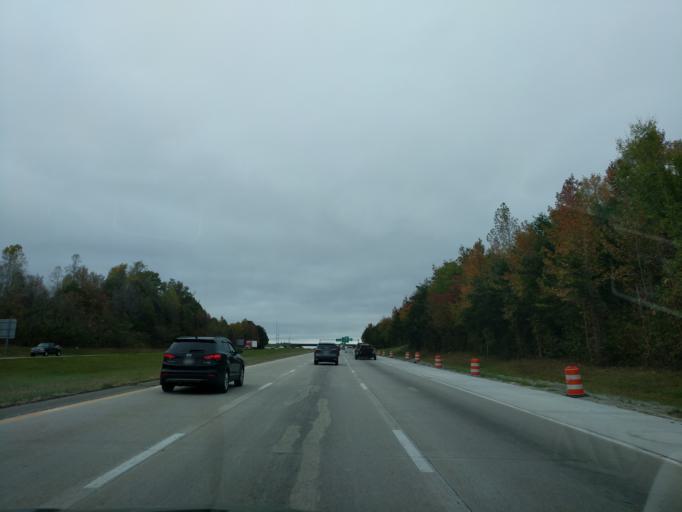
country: US
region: North Carolina
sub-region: Randolph County
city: Archdale
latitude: 35.9185
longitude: -79.9427
